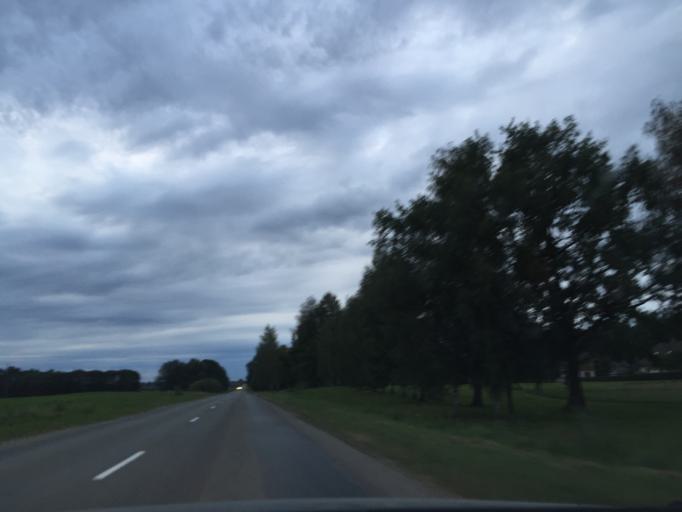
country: LV
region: Vecumnieki
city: Vecumnieki
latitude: 56.5140
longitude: 24.5612
